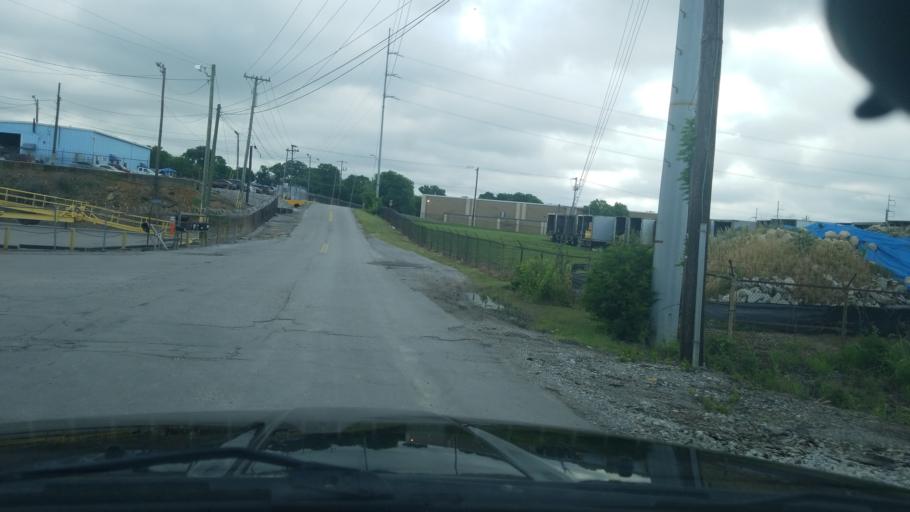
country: US
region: Tennessee
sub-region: Davidson County
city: Oak Hill
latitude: 36.0985
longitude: -86.7511
